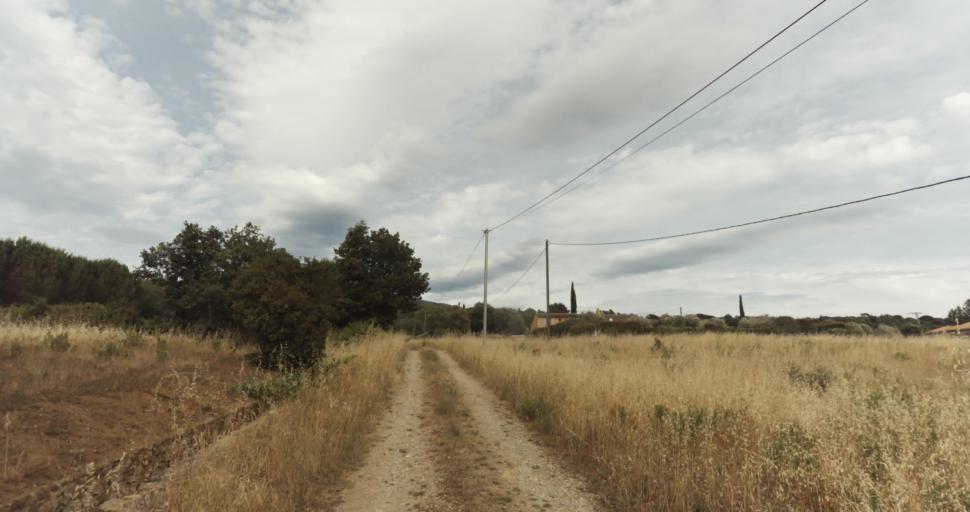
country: FR
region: Provence-Alpes-Cote d'Azur
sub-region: Departement du Var
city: Gassin
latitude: 43.2160
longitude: 6.5790
